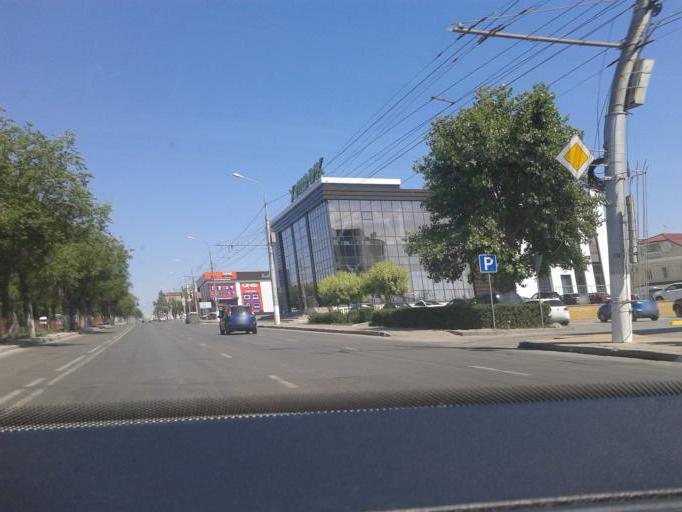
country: RU
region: Volgograd
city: Volgograd
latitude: 48.7277
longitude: 44.4993
